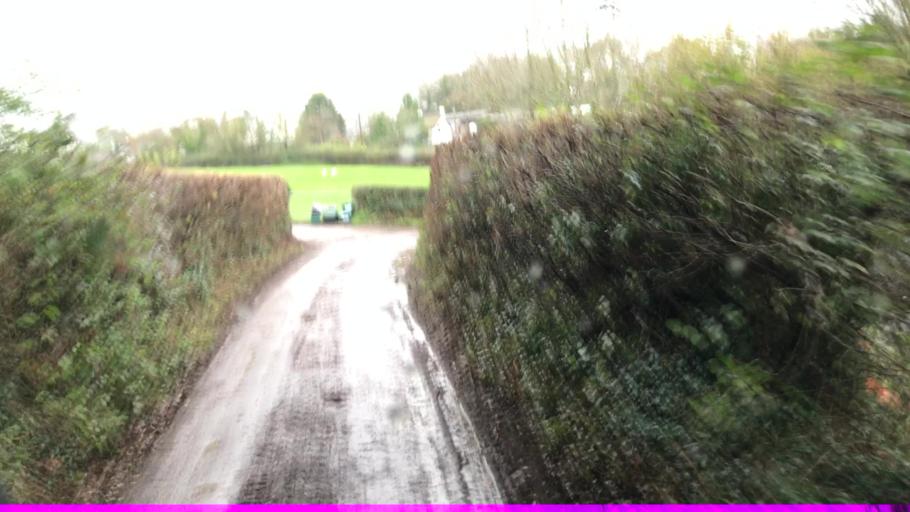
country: GB
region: England
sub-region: Devon
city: Chudleigh
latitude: 50.6325
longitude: -3.6159
